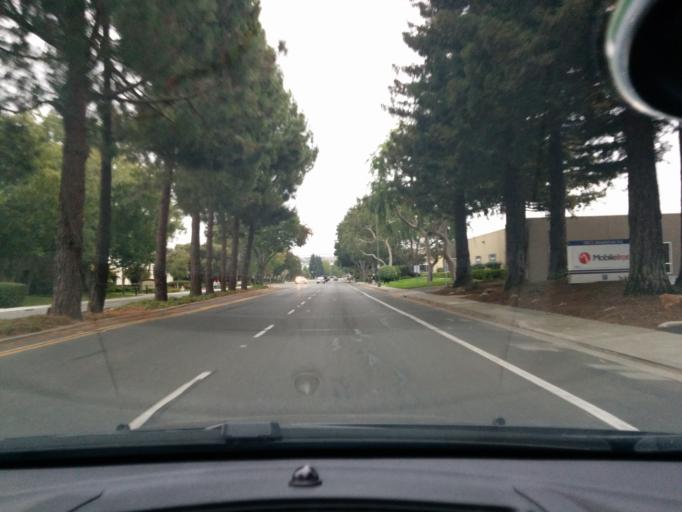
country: US
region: California
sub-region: Santa Clara County
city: Mountain View
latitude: 37.3969
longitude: -122.0586
